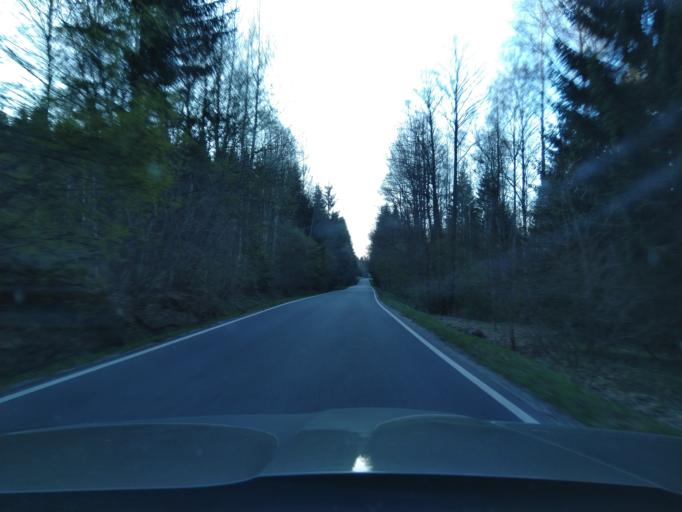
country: CZ
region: Jihocesky
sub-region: Okres Prachatice
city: Vimperk
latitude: 48.9522
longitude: 13.7800
